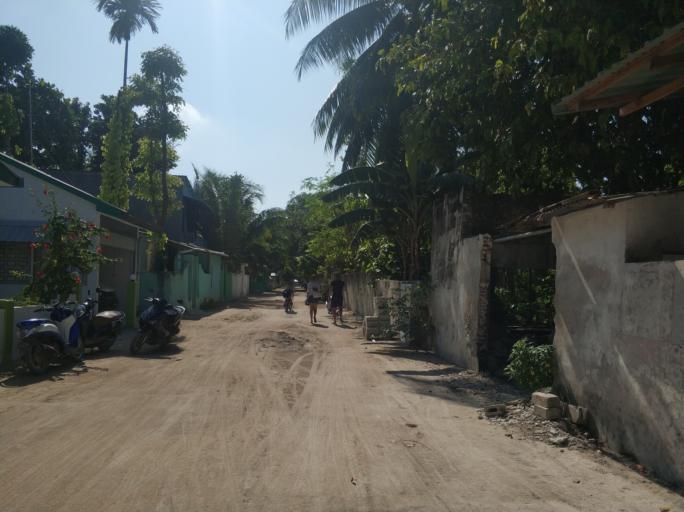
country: MV
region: Maale
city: Male
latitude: 4.4384
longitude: 72.9617
